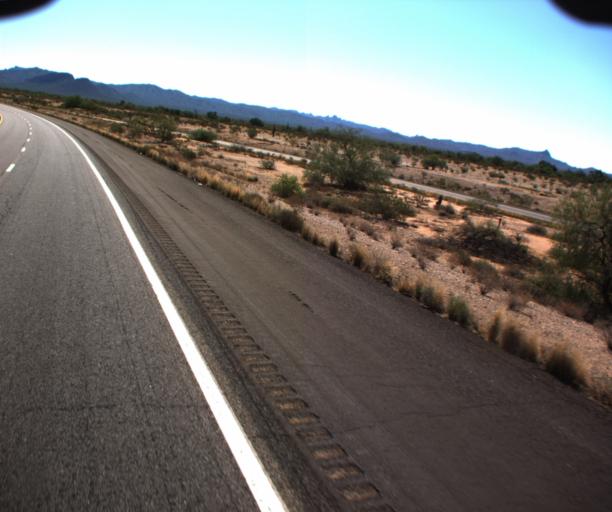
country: US
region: Arizona
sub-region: Pinal County
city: Gold Camp
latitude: 33.2552
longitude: -111.3345
